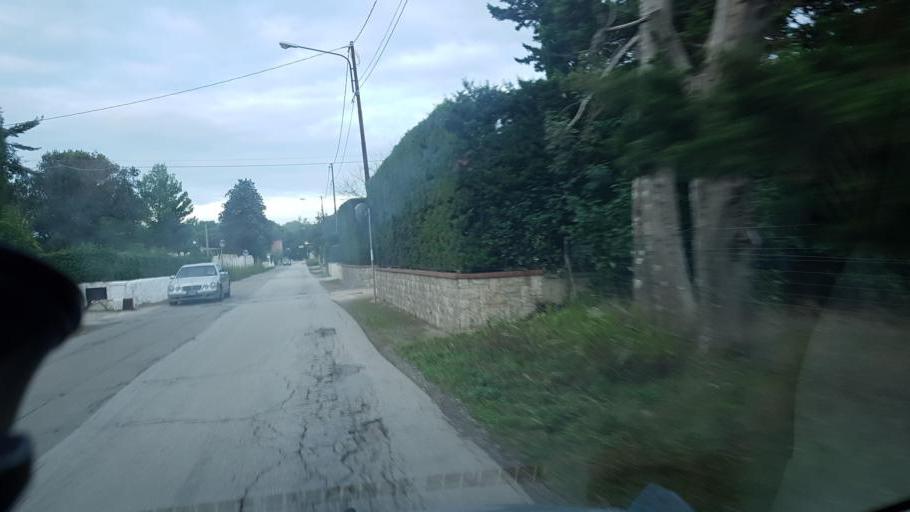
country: IT
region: Apulia
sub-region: Provincia di Brindisi
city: Latiano
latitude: 40.5454
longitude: 17.7033
